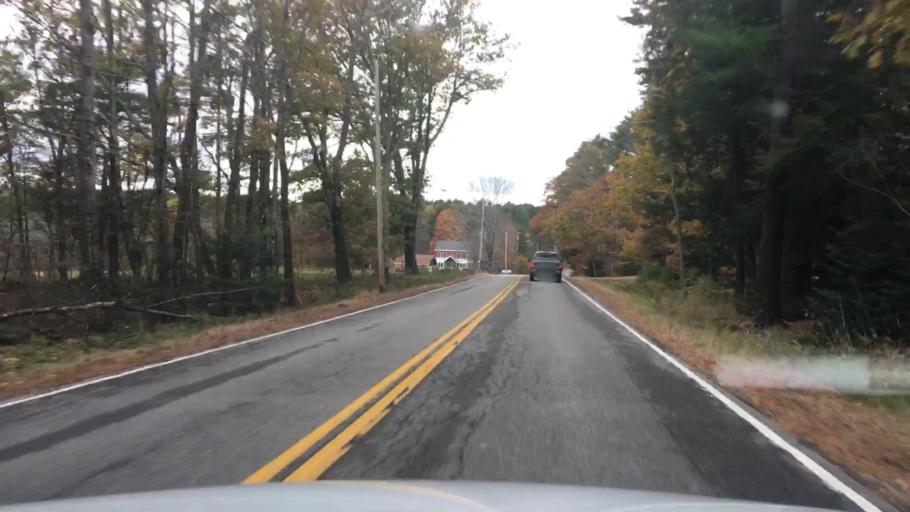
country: US
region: Maine
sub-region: Sagadahoc County
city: Richmond
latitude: 44.1278
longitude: -69.9075
